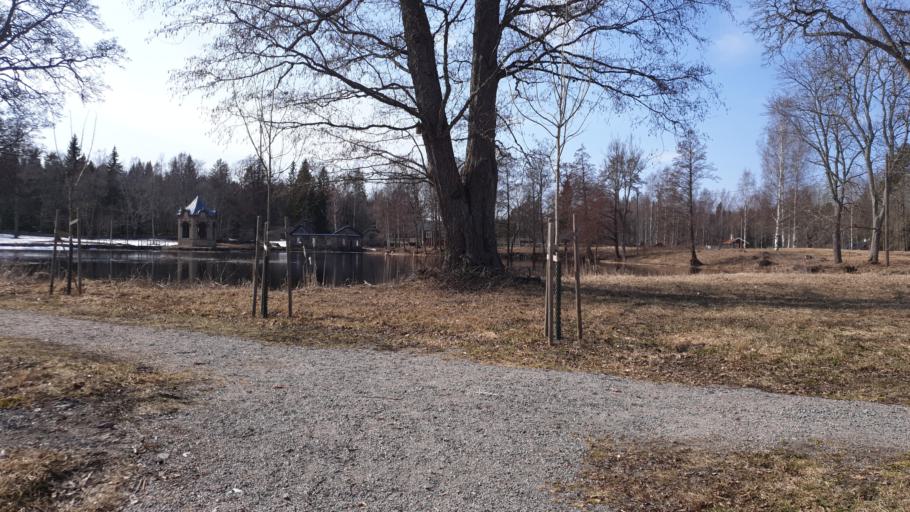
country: SE
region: Gaevleborg
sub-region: Gavle Kommun
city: Norrsundet
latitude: 61.0465
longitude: 17.1433
